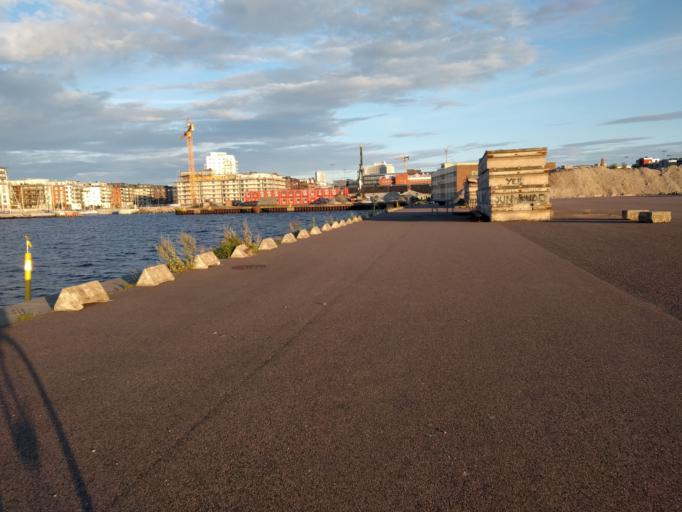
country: SE
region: Skane
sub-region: Malmo
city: Malmoe
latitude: 55.6201
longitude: 12.9844
